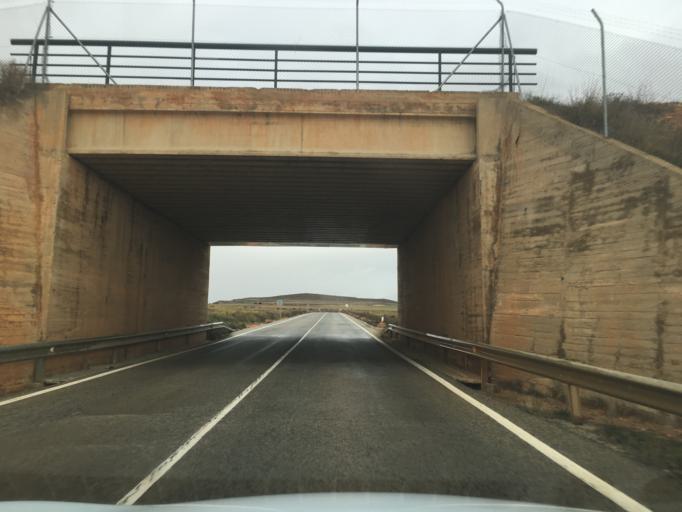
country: ES
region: Castille-La Mancha
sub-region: Provincia de Albacete
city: Chinchilla de Monte Aragon
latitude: 38.8959
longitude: -1.6850
